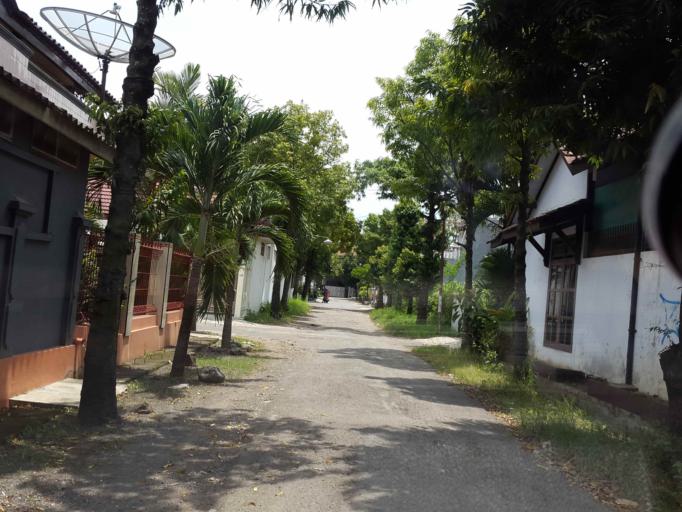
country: ID
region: Central Java
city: Pemalang
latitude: -6.8993
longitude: 109.3877
